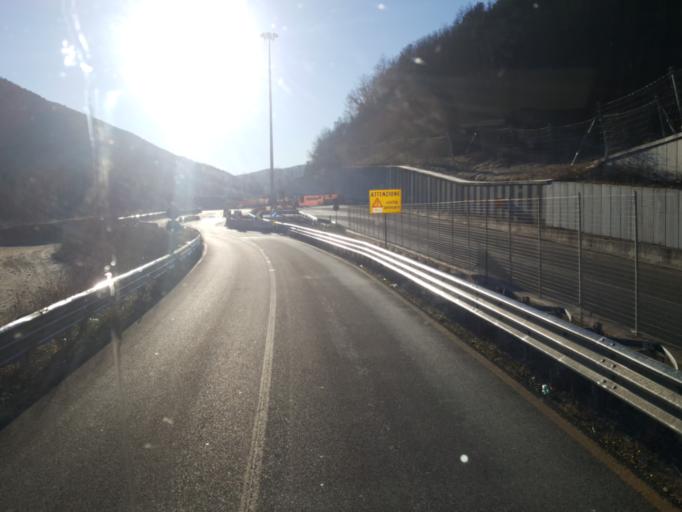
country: IT
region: Latium
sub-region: Provincia di Rieti
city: Colli sul Velino
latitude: 42.5273
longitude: 12.7310
